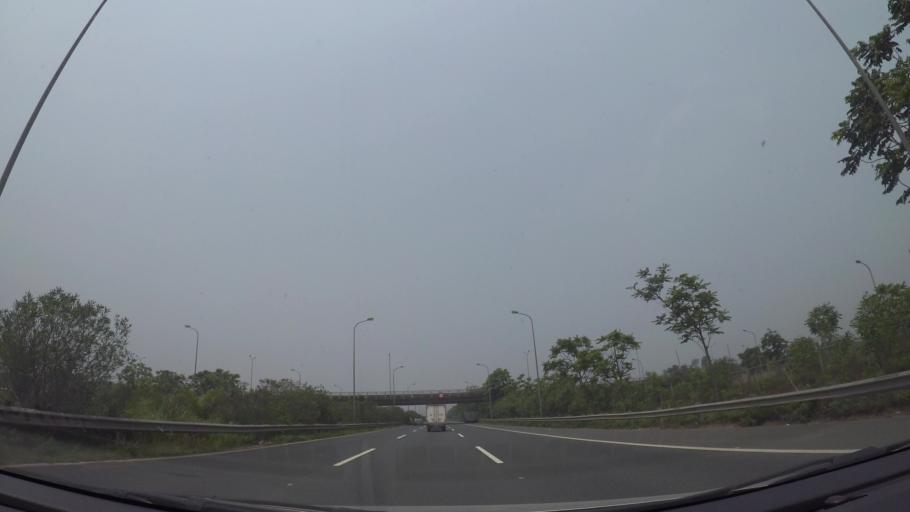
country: VN
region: Ha Noi
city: Lien Quan
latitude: 20.9905
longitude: 105.5372
